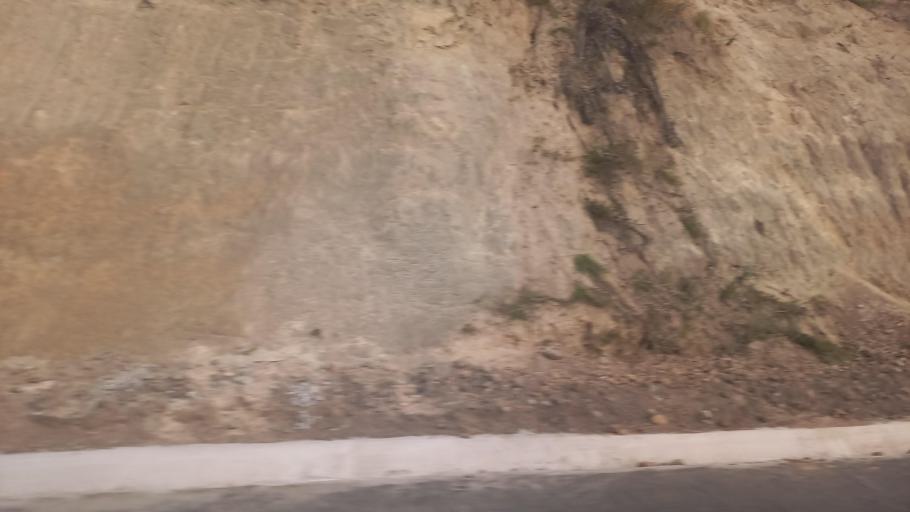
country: EC
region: Pichincha
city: Cayambe
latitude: 0.1275
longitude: -78.0729
